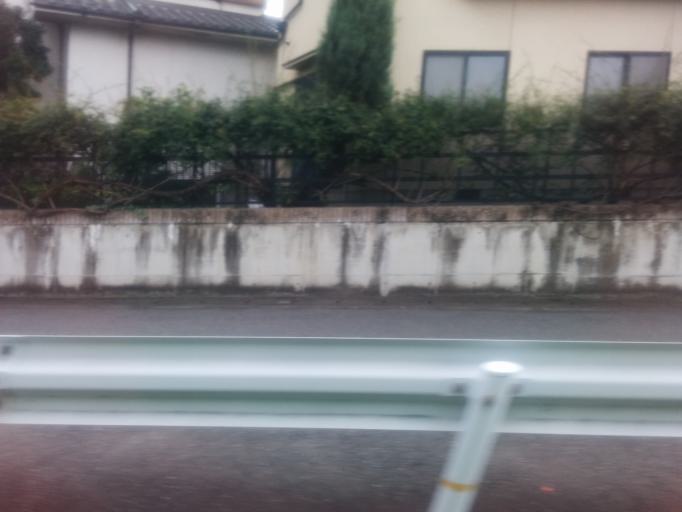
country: JP
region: Kyoto
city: Uji
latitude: 34.9389
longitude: 135.7685
